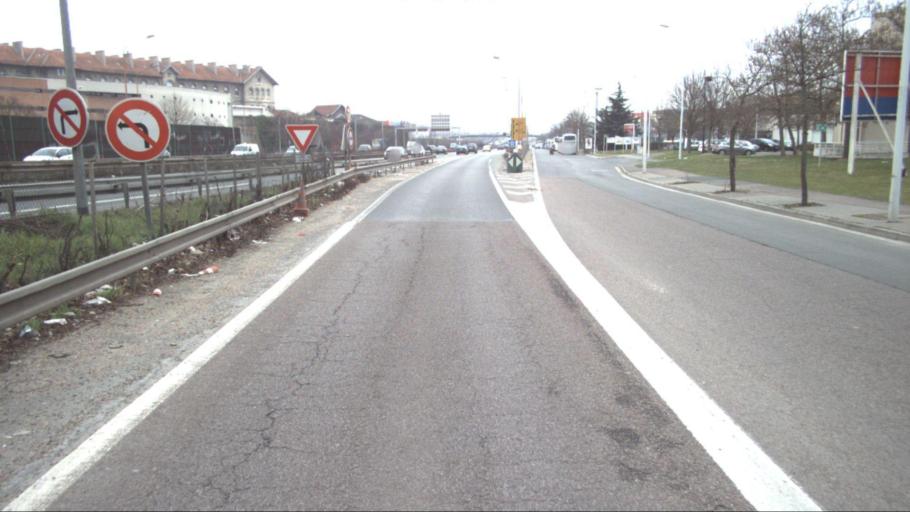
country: FR
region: Ile-de-France
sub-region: Departement du Val-d'Oise
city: Bezons
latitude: 48.9167
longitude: 2.2212
